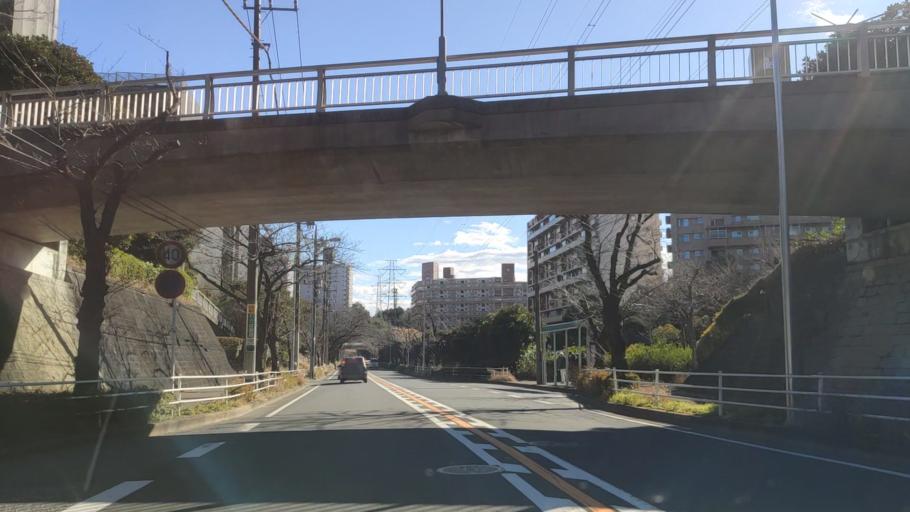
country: JP
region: Kanagawa
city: Minami-rinkan
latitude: 35.5064
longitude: 139.5032
